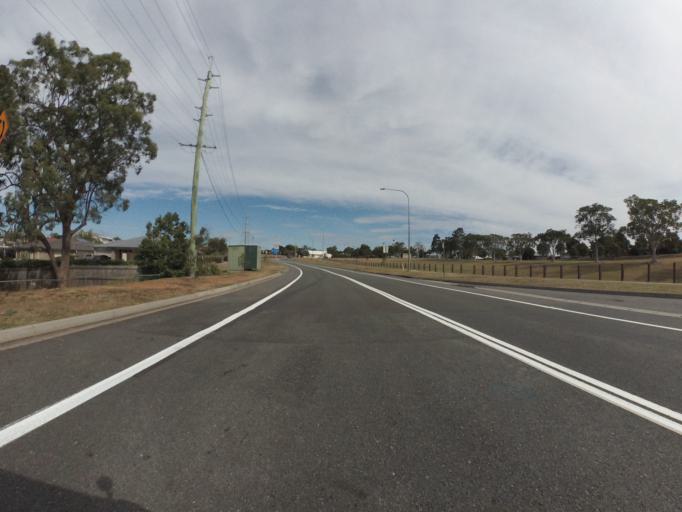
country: AU
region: Queensland
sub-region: Brisbane
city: Moggill
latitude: -27.5706
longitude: 152.8742
